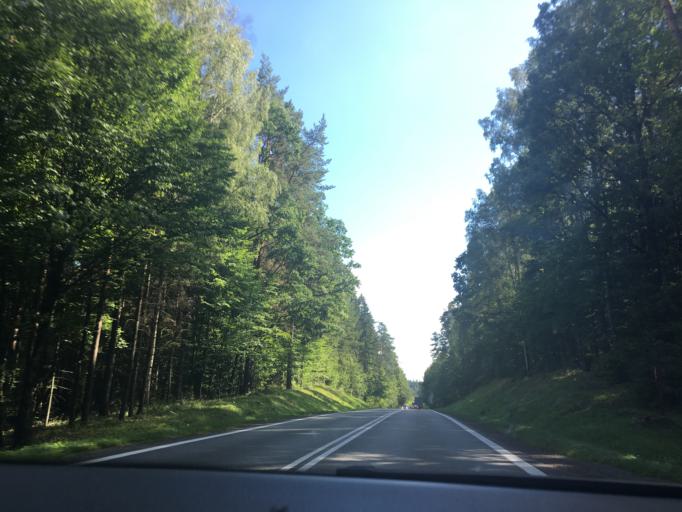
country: PL
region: Podlasie
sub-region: Powiat bialostocki
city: Wasilkow
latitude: 53.2851
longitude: 23.1220
